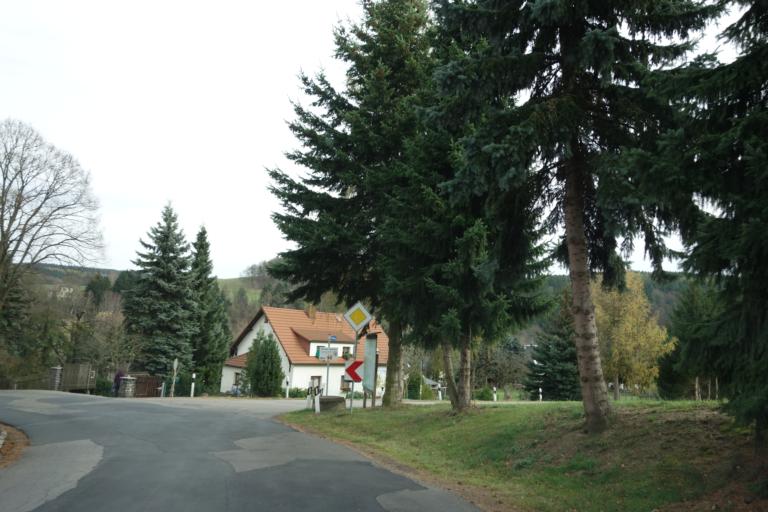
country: DE
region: Saxony
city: Leubsdorf
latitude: 50.8184
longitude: 13.1372
